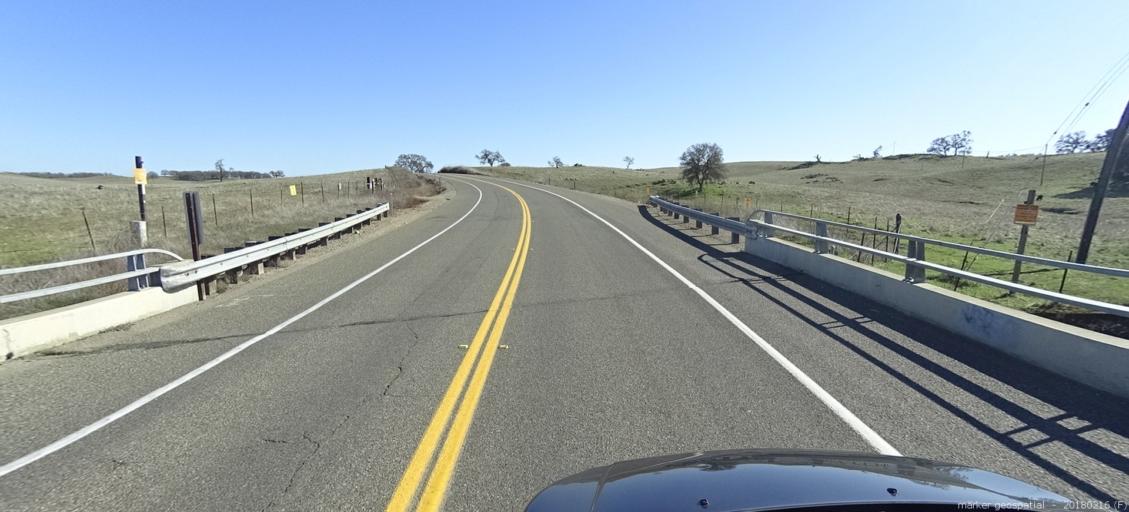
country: US
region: California
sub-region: Sacramento County
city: Rancho Murieta
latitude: 38.5628
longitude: -121.1276
